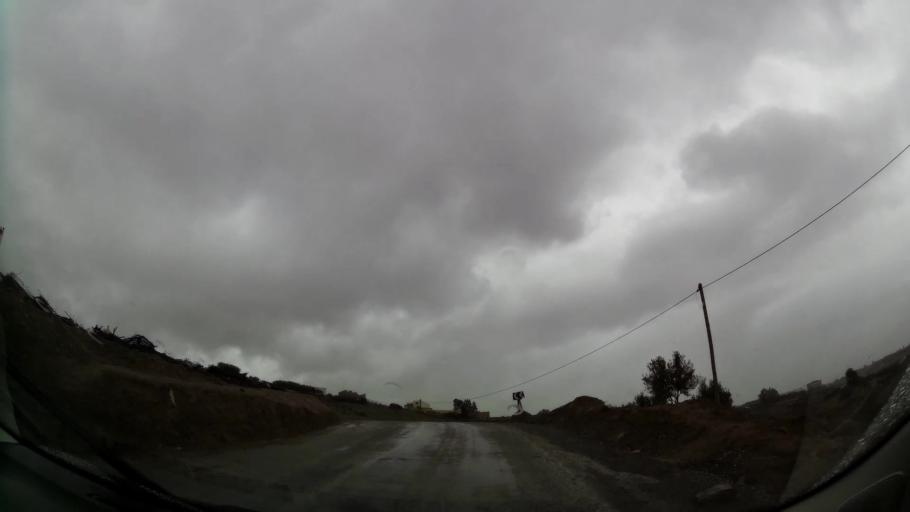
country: MA
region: Oriental
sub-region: Nador
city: Midar
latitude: 34.8907
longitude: -3.7443
